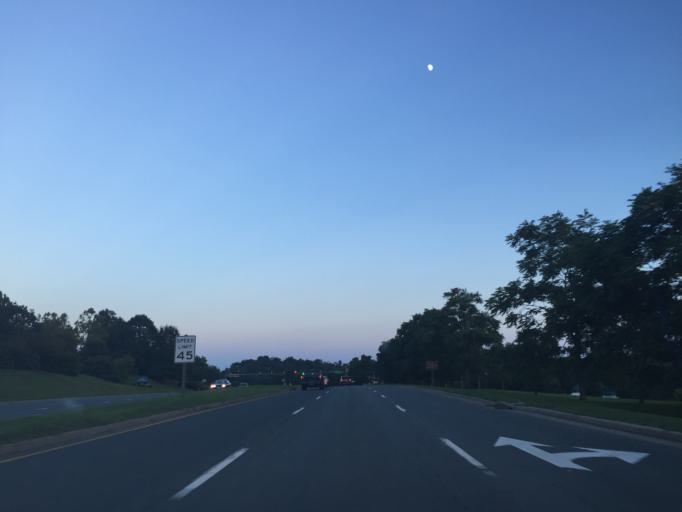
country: US
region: Virginia
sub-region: City of Charlottesville
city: Charlottesville
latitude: 38.0281
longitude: -78.4404
